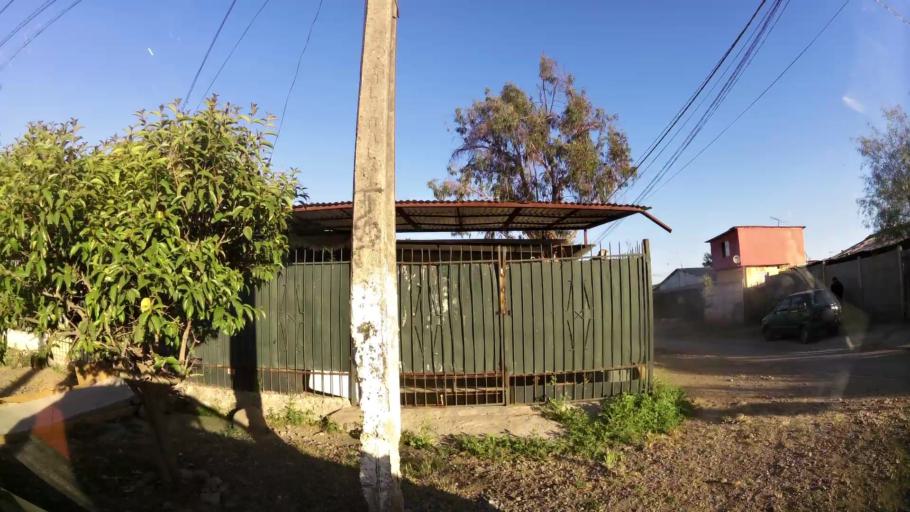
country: CL
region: Santiago Metropolitan
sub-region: Provincia de Maipo
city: San Bernardo
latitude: -33.5810
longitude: -70.6921
